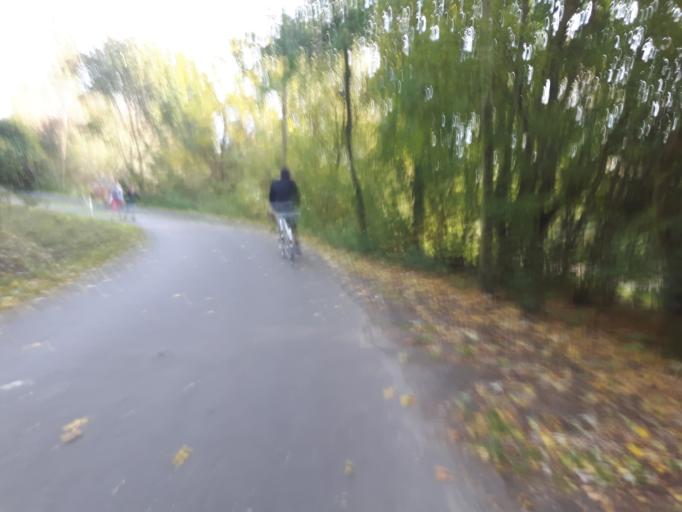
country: DE
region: Berlin
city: Spandau
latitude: 52.5414
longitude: 13.1860
